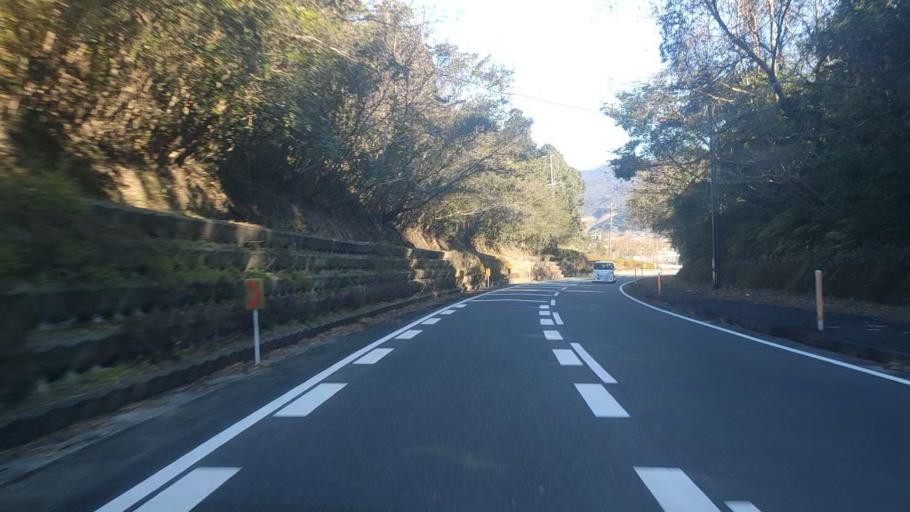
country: JP
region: Miyazaki
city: Nobeoka
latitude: 32.7045
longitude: 131.8159
